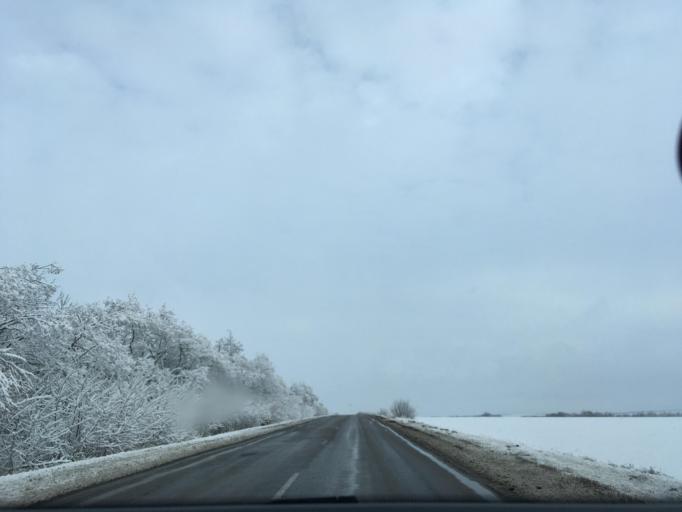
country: UA
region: Luhansk
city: Lozno-Oleksandrivka
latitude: 49.9912
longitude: 39.0221
